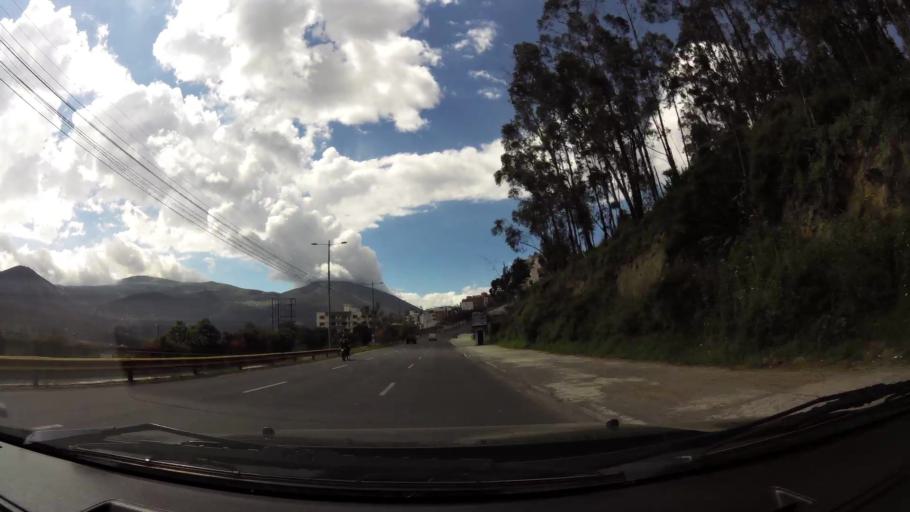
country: EC
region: Pichincha
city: Quito
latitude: -0.0990
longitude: -78.4853
